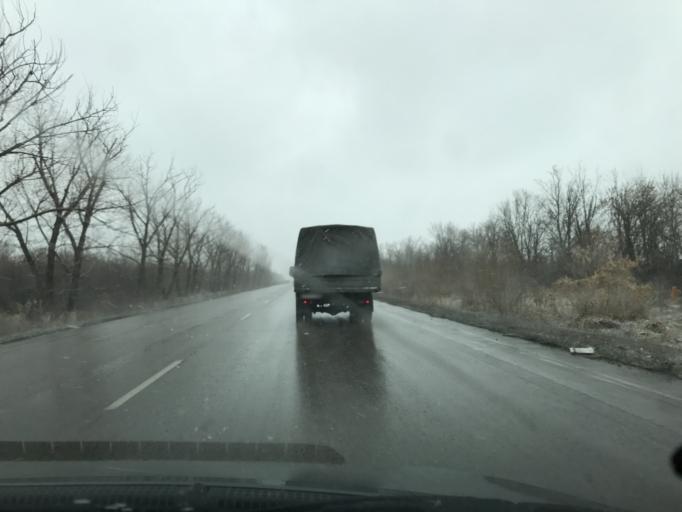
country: RU
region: Rostov
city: Bataysk
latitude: 47.0677
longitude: 39.8020
